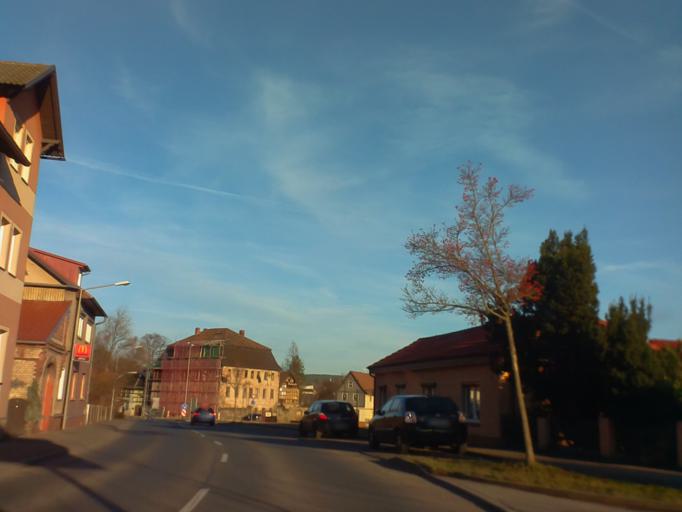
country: DE
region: Thuringia
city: Bad Blankenburg
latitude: 50.6857
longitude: 11.3138
